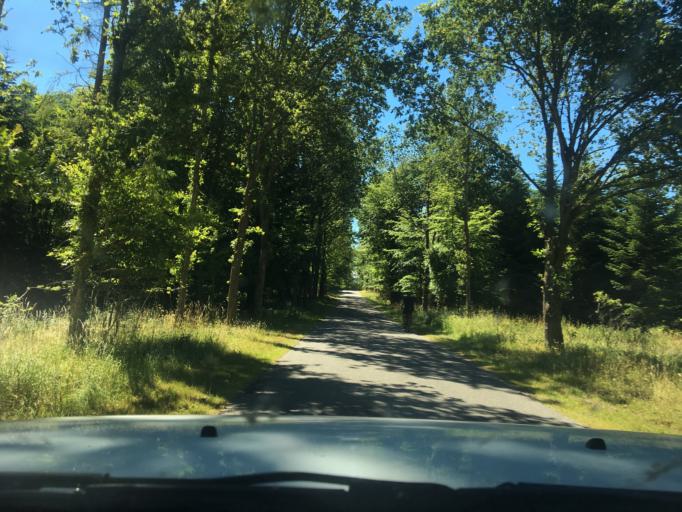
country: DK
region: Central Jutland
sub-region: Norddjurs Kommune
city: Auning
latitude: 56.3583
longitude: 10.3900
